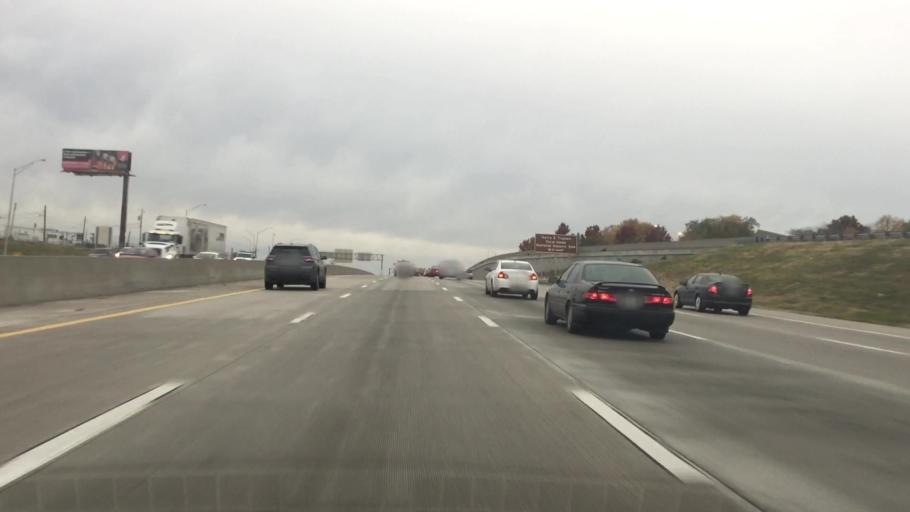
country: US
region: Missouri
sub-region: Jackson County
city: Grandview
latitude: 38.9152
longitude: -94.5263
